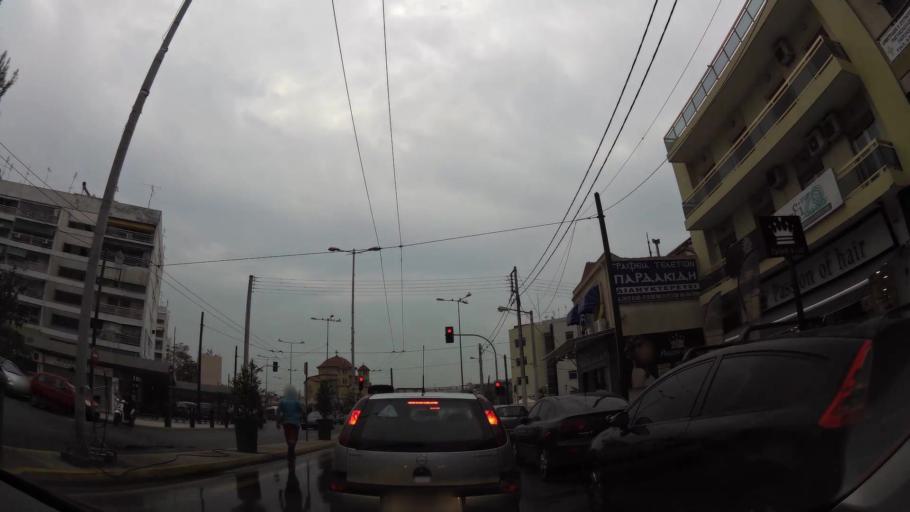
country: GR
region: Attica
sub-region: Nomarchia Athinas
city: Peristeri
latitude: 38.0139
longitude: 23.6948
